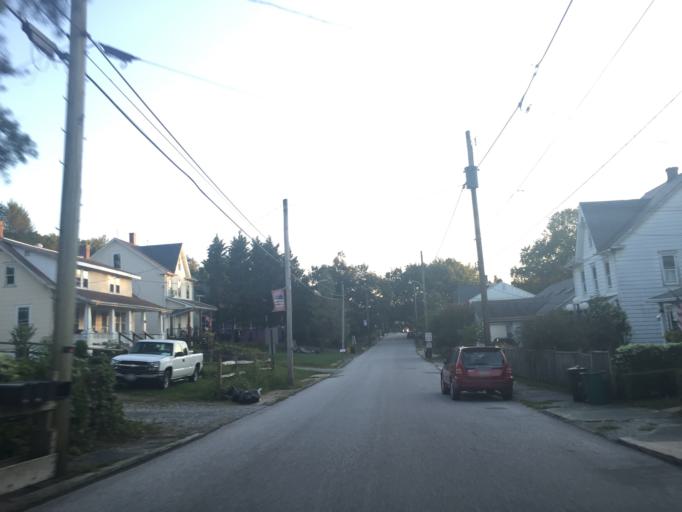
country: US
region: Pennsylvania
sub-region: York County
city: Susquehanna Trails
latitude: 39.7244
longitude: -76.3317
